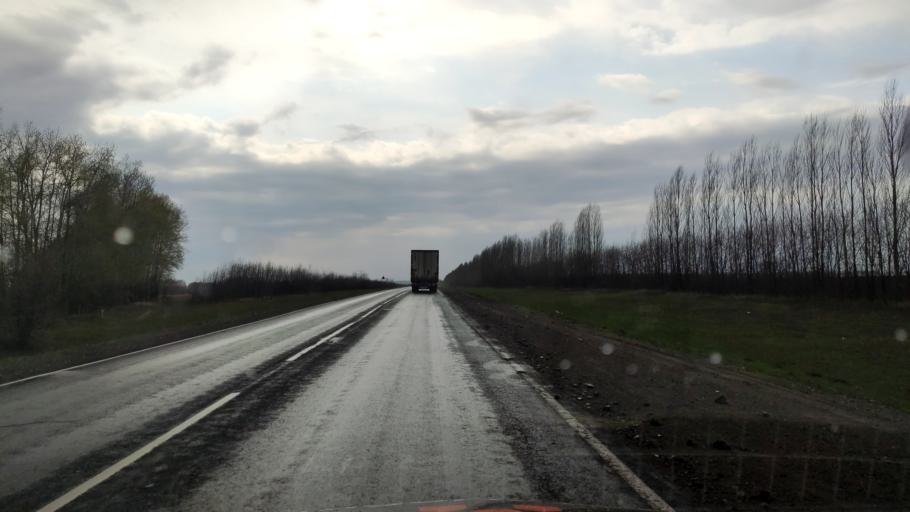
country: RU
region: Voronezj
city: Nizhnedevitsk
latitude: 51.5724
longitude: 38.2940
